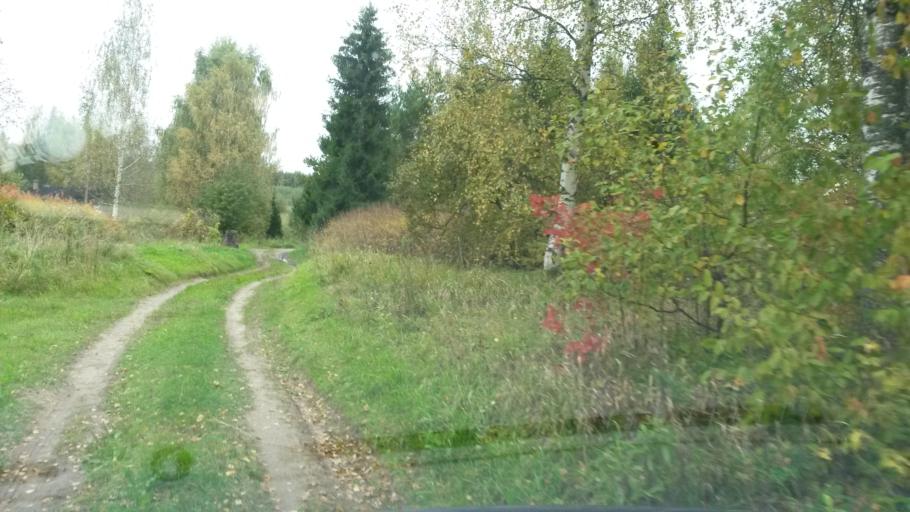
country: RU
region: Jaroslavl
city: Tutayev
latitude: 57.9502
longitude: 39.4261
